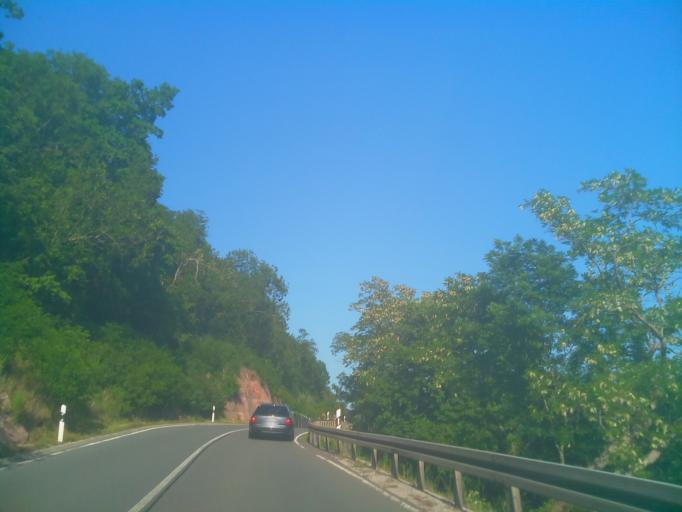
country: DE
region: Thuringia
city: Reinstadt
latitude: 50.7429
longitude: 11.4534
